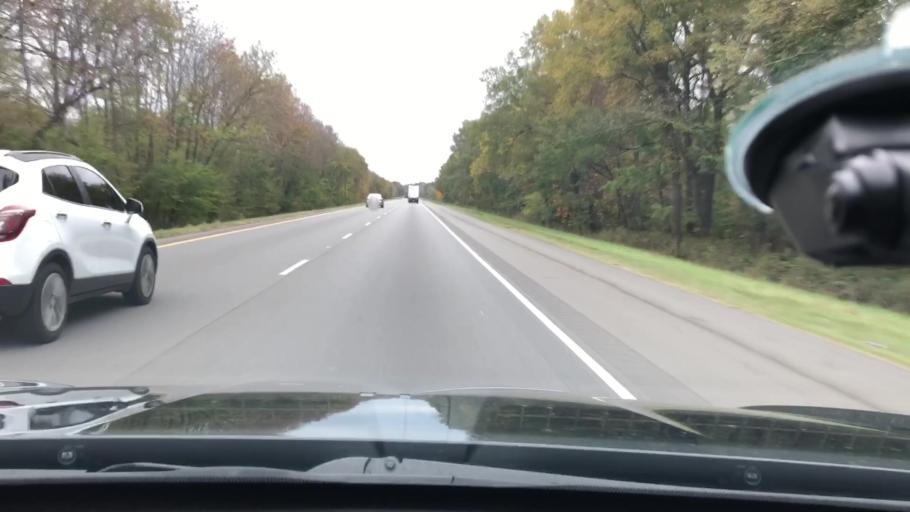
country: US
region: Arkansas
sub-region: Hempstead County
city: Hope
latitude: 33.6554
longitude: -93.6567
